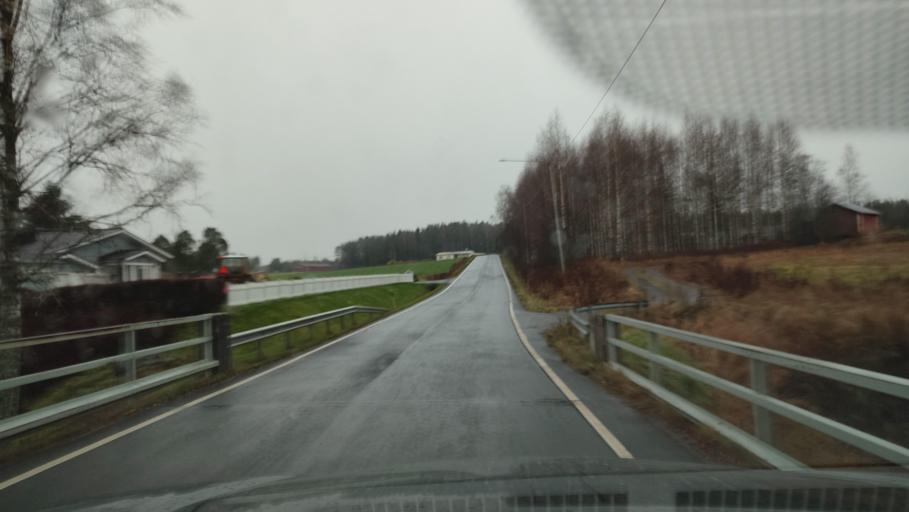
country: FI
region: Southern Ostrobothnia
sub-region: Suupohja
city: Karijoki
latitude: 62.1338
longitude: 21.6798
